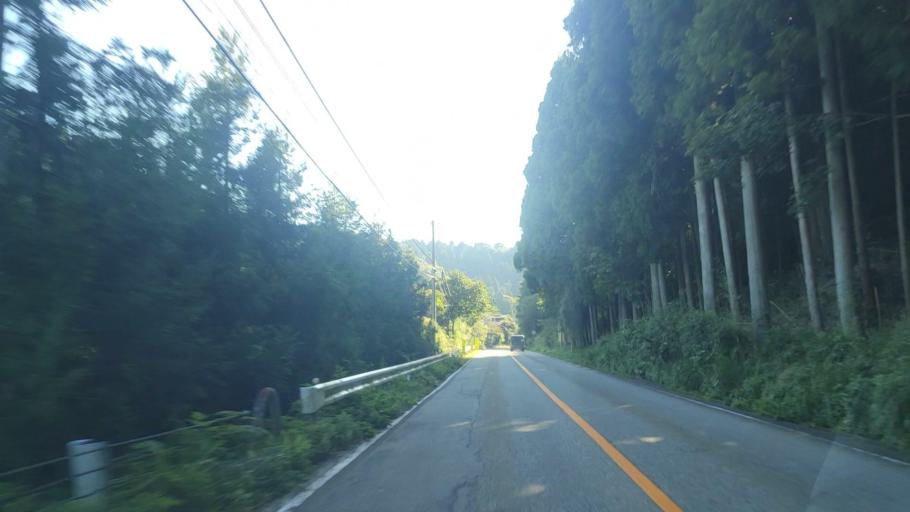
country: JP
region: Ishikawa
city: Nanao
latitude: 37.1406
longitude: 136.8685
